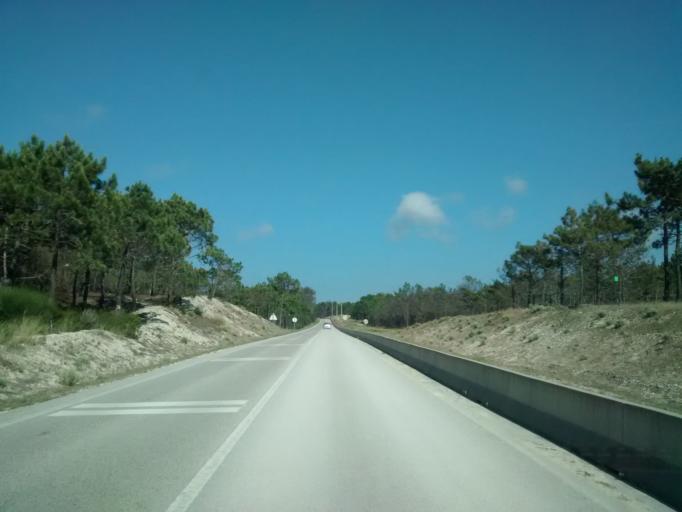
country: PT
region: Coimbra
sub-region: Figueira da Foz
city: Lavos
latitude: 40.0017
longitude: -8.9073
